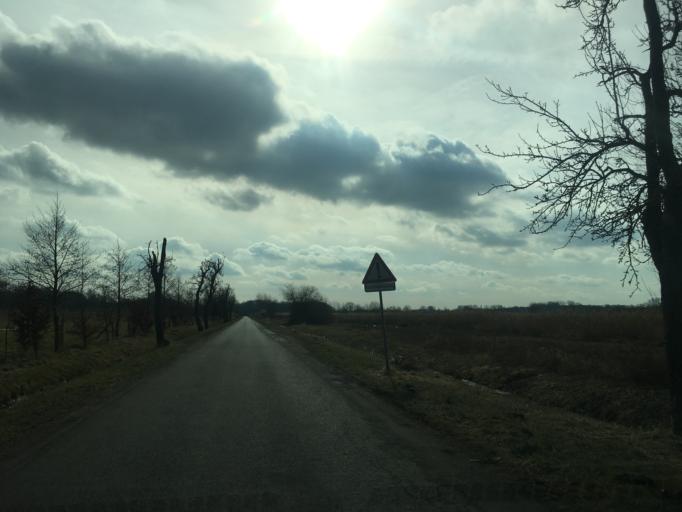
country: DE
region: North Rhine-Westphalia
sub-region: Regierungsbezirk Munster
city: Greven
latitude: 52.0471
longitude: 7.6408
